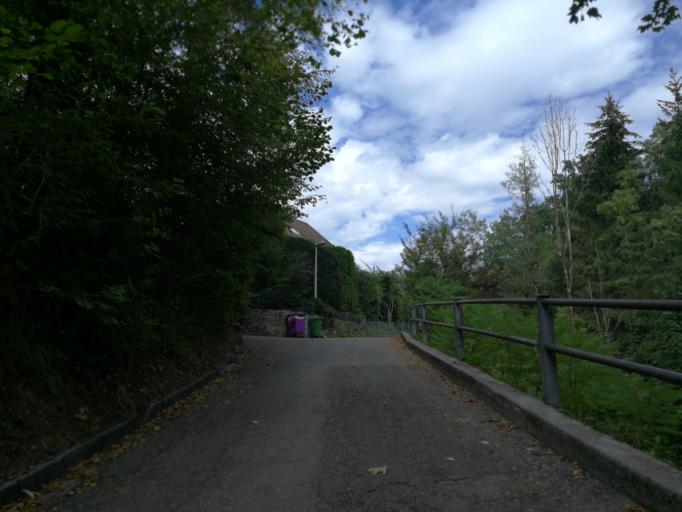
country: CH
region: Zurich
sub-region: Bezirk Meilen
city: Feldmeilen
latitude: 47.2835
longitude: 8.6248
